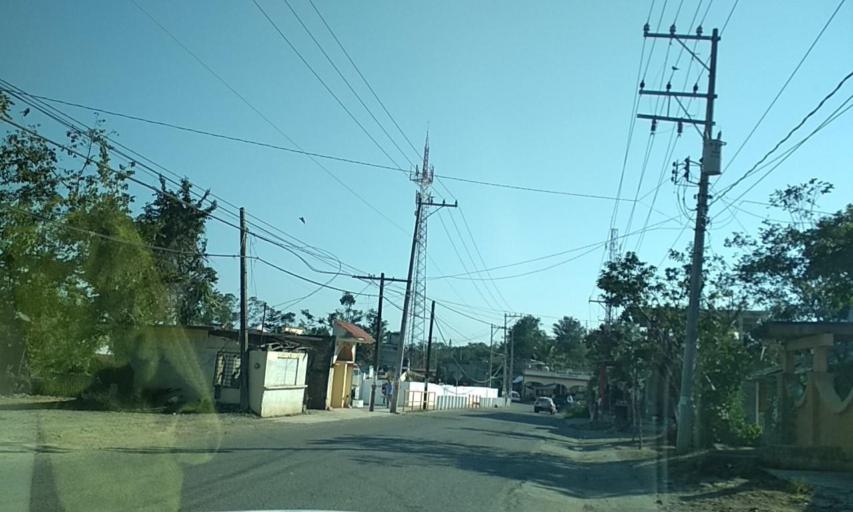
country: MX
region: Veracruz
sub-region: Papantla
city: El Chote
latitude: 20.4064
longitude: -97.3377
